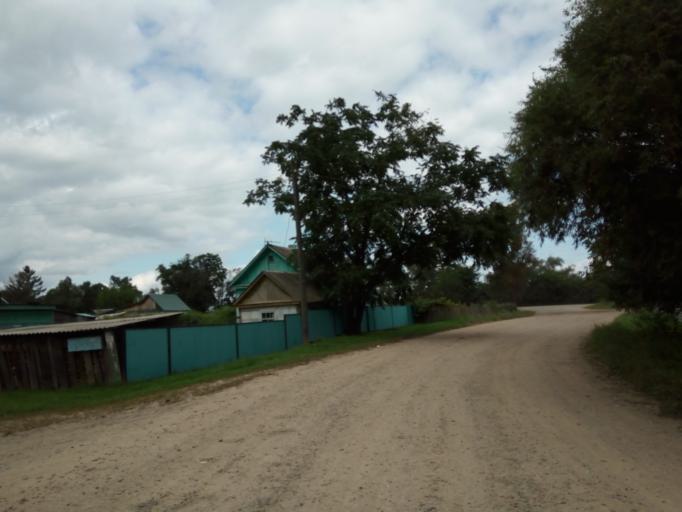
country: RU
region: Primorskiy
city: Dal'nerechensk
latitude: 45.9357
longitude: 133.8148
